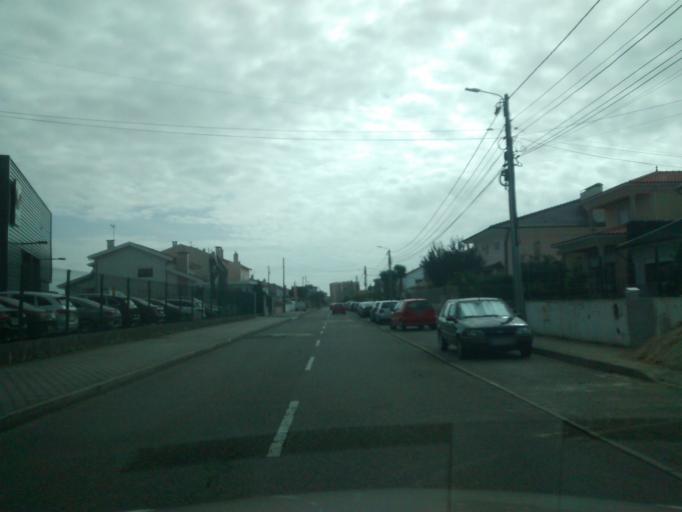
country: PT
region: Aveiro
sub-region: Aveiro
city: Aveiro
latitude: 40.6579
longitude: -8.6174
